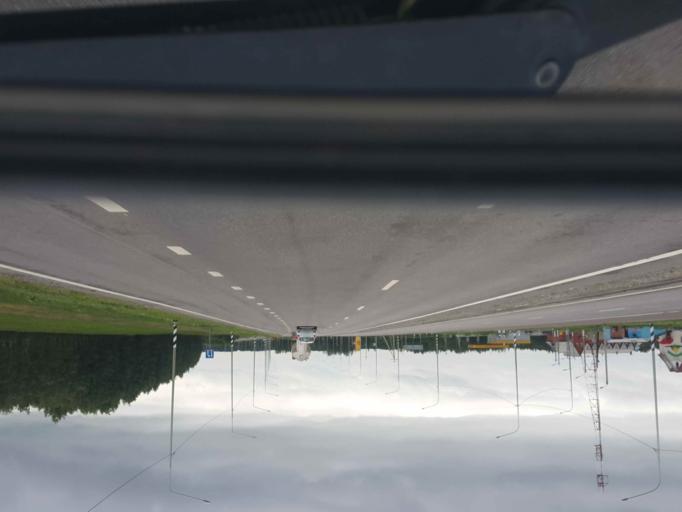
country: RU
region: Tambov
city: Zavoronezhskoye
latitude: 52.8604
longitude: 40.7686
